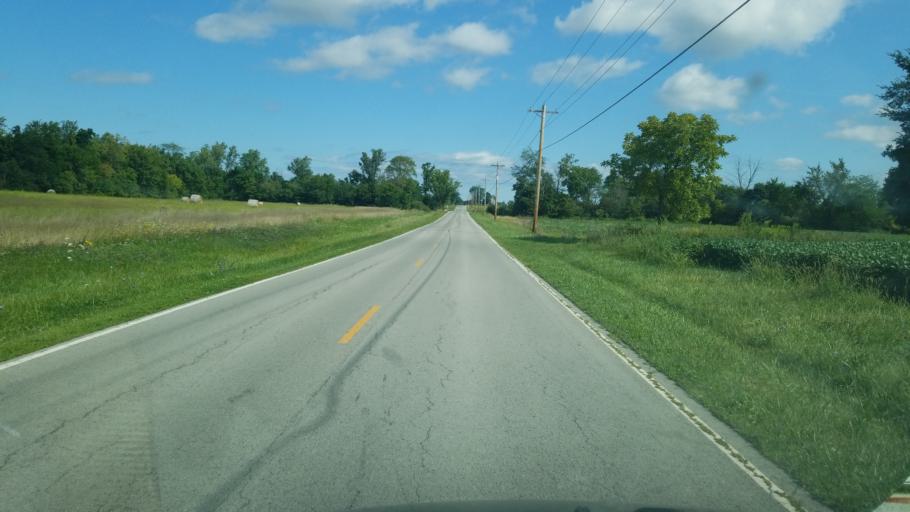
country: US
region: Ohio
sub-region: Seneca County
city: Fostoria
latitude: 41.1031
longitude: -83.4401
